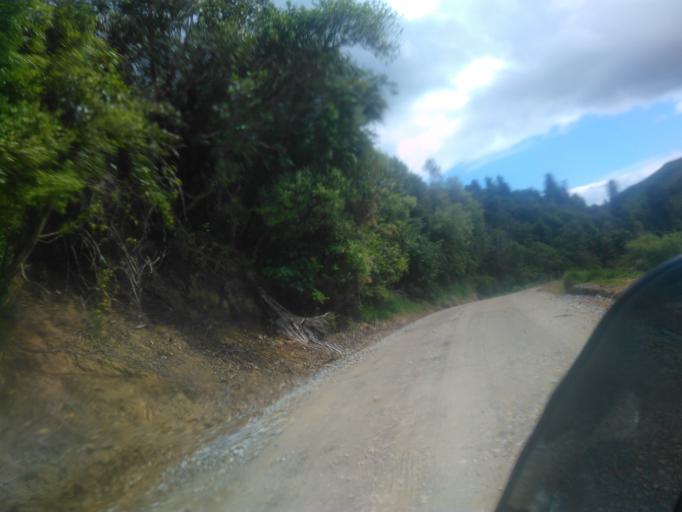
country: NZ
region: Hawke's Bay
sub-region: Wairoa District
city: Wairoa
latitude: -38.7631
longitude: 177.5909
